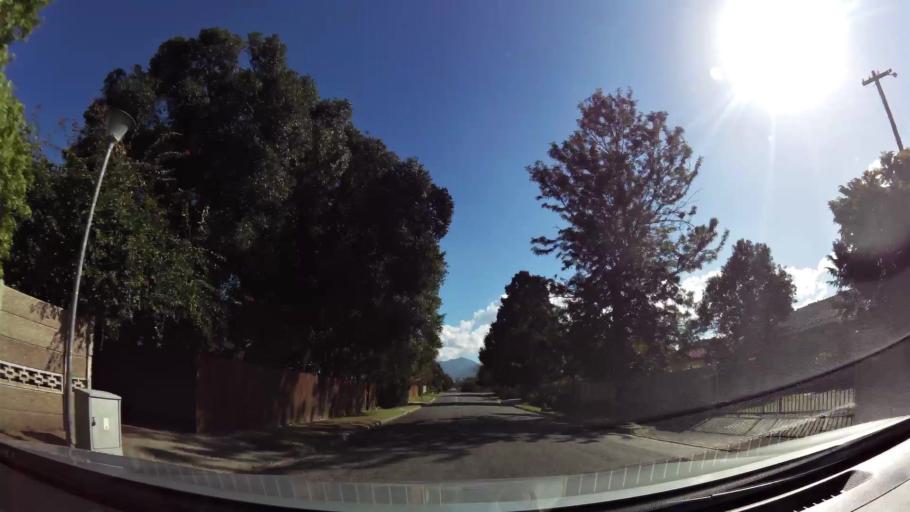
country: ZA
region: Western Cape
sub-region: Eden District Municipality
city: George
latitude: -33.9648
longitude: 22.4498
